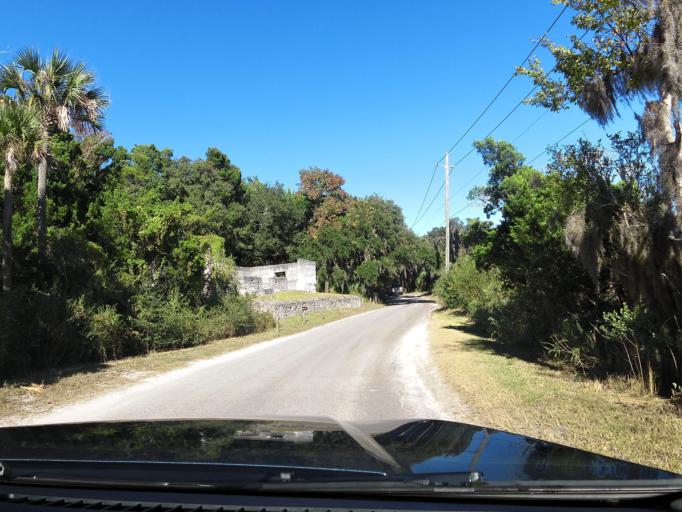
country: US
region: Florida
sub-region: Duval County
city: Atlantic Beach
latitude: 30.4091
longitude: -81.4313
